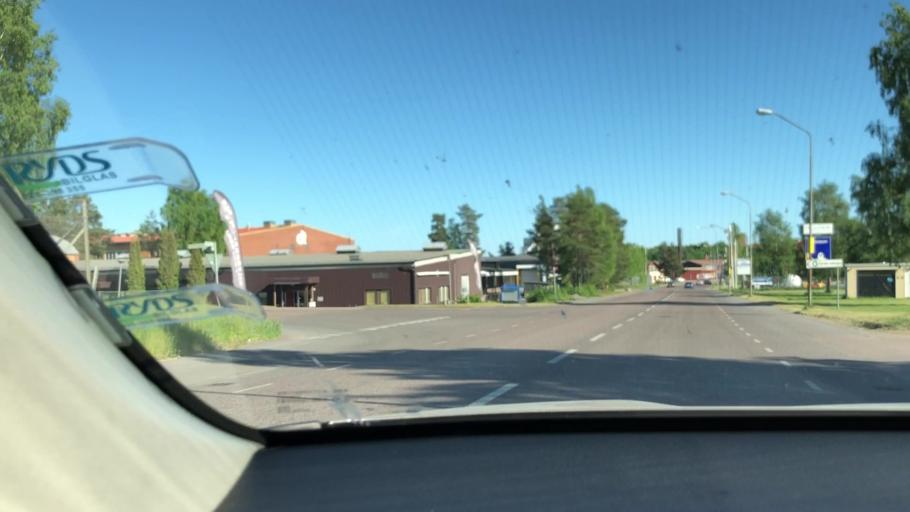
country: SE
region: Dalarna
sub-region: Faluns Kommun
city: Falun
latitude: 60.6067
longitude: 15.6004
